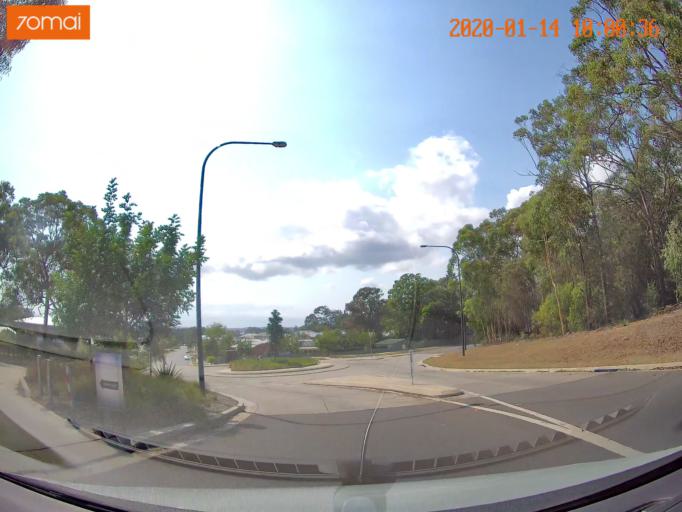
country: AU
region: New South Wales
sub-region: Wyong Shire
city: Kingfisher Shores
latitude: -33.1230
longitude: 151.5331
